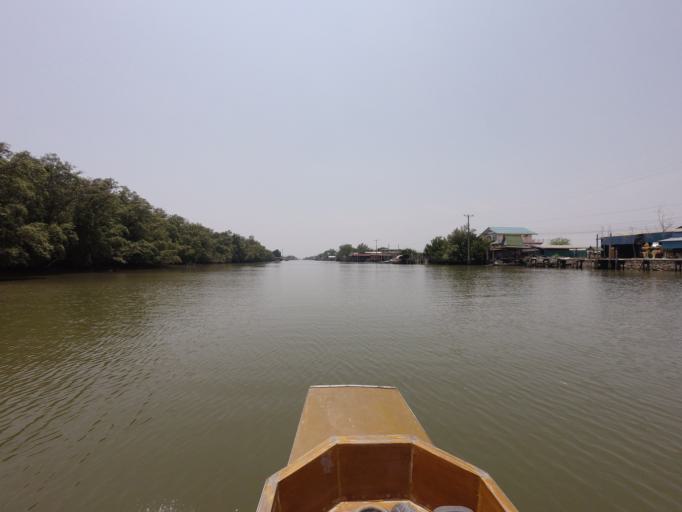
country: TH
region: Bangkok
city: Thung Khru
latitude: 13.5448
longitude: 100.4780
